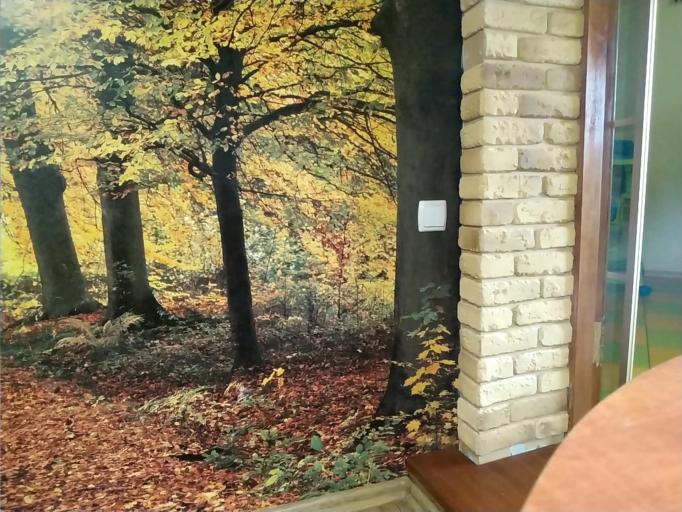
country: RU
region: Smolensk
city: Dorogobuzh
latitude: 54.8568
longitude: 33.3169
